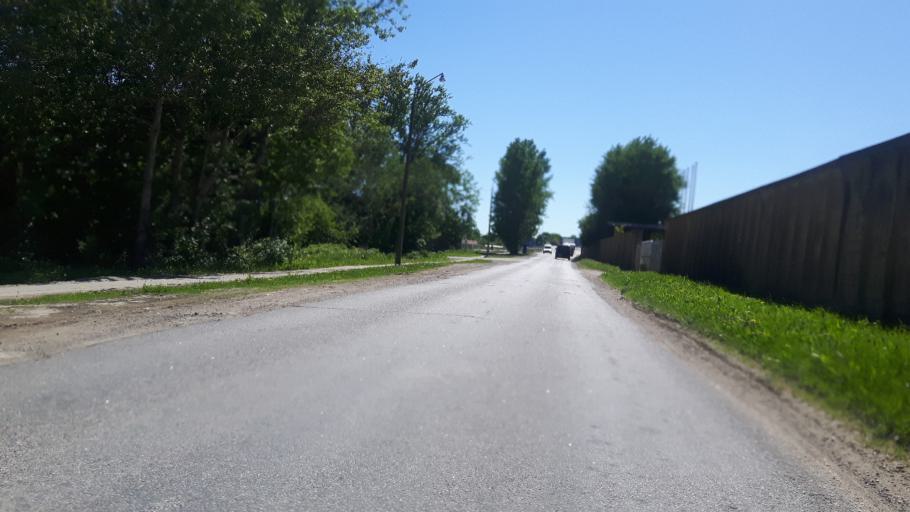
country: EE
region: Ida-Virumaa
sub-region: Sillamaee linn
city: Sillamae
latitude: 59.3933
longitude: 27.7492
